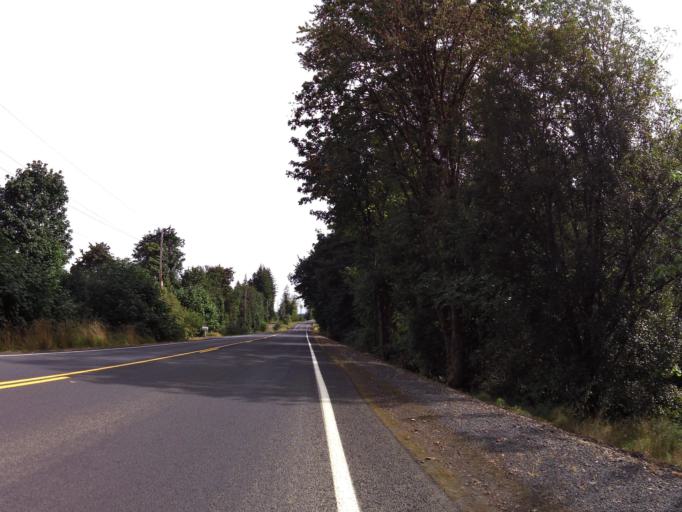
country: US
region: Washington
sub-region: Cowlitz County
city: Castle Rock
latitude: 46.3353
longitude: -122.9343
